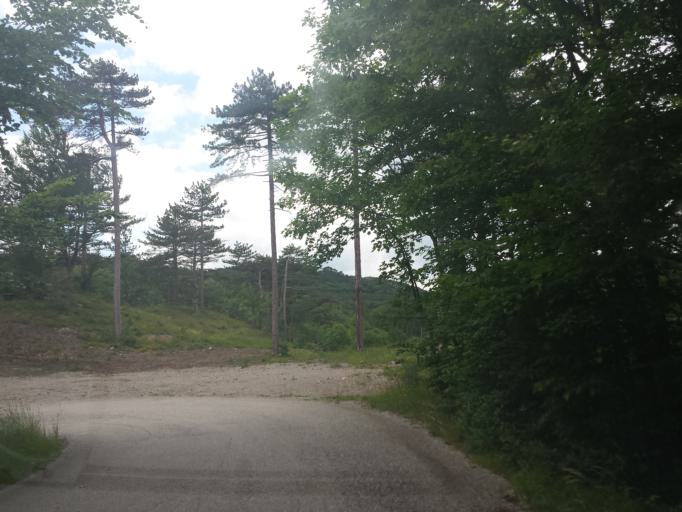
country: AT
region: Lower Austria
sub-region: Politischer Bezirk Baden
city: Hirtenberg
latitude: 47.9226
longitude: 16.1443
